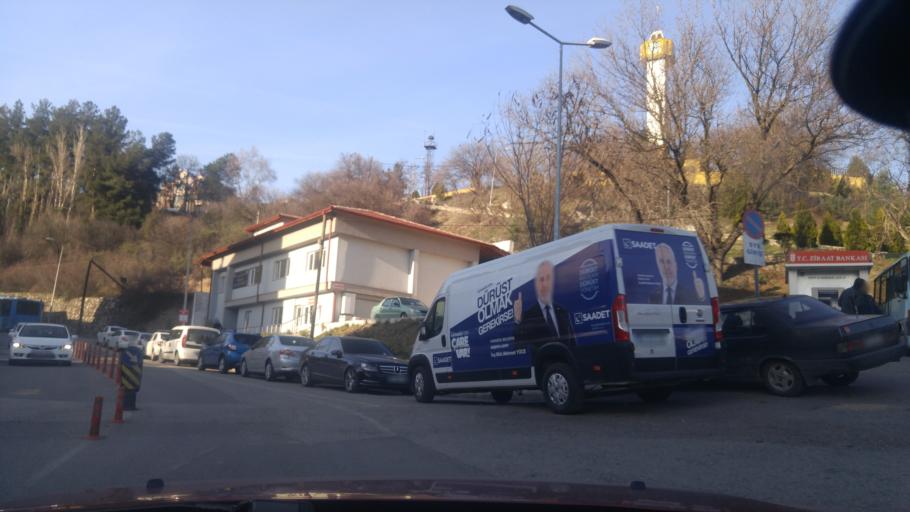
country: TR
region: Karabuk
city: Karabuk
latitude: 41.1977
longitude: 32.6178
